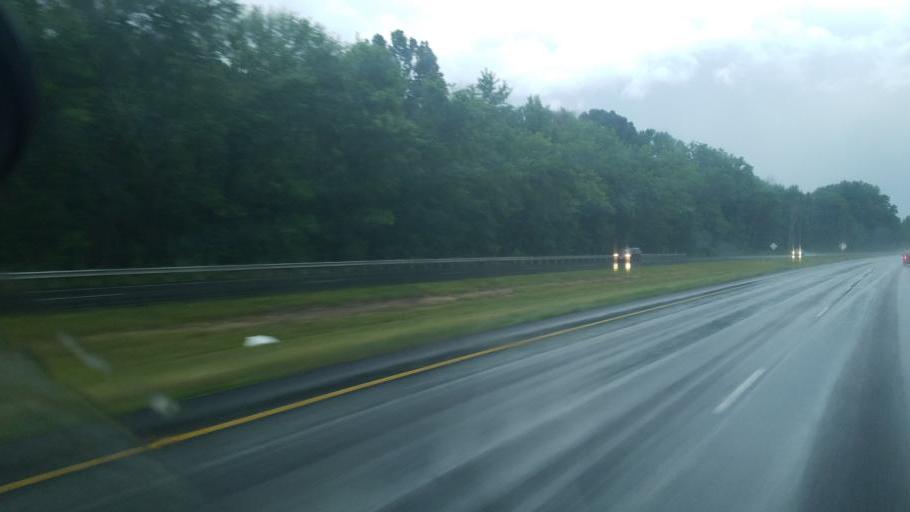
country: US
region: Ohio
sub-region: Summit County
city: Norton
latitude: 41.0671
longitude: -81.6628
